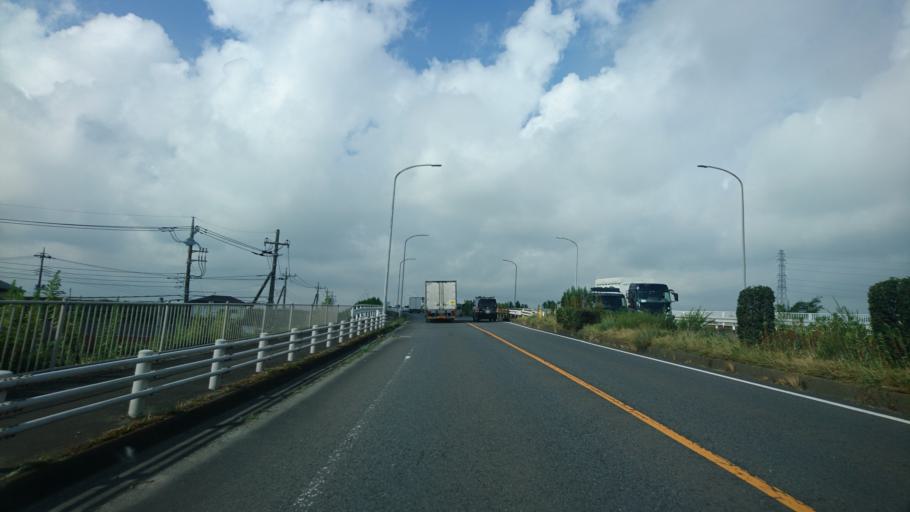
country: JP
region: Gunma
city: Tatebayashi
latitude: 36.2925
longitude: 139.5295
